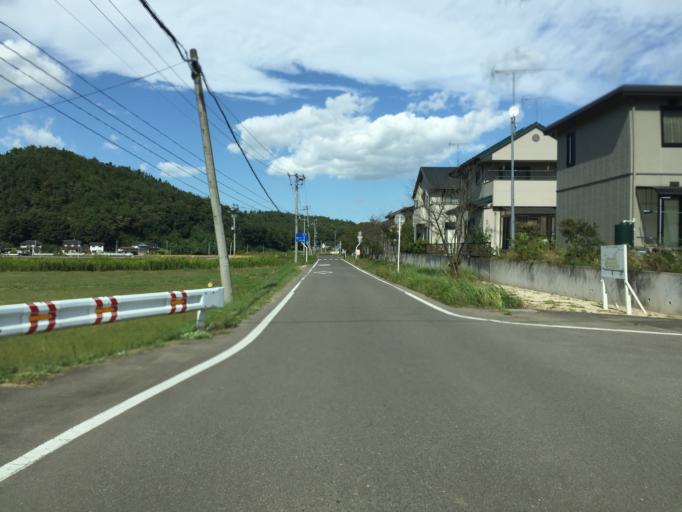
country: JP
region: Fukushima
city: Hobaramachi
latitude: 37.7814
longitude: 140.5501
